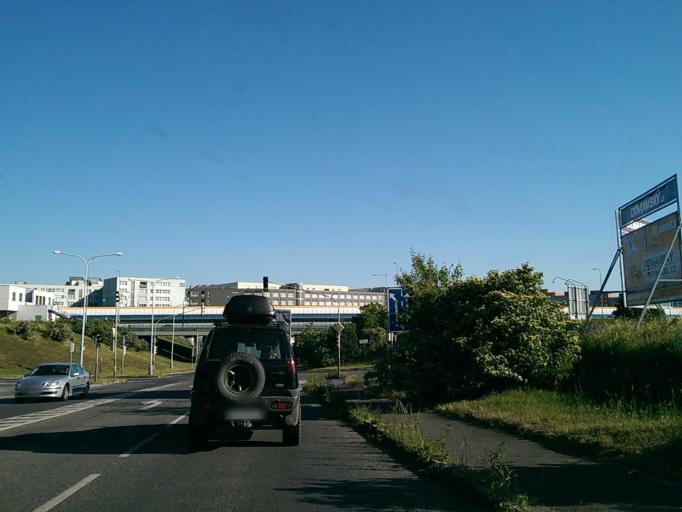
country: CZ
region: Praha
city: Cerny Most
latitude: 50.1104
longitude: 14.5745
